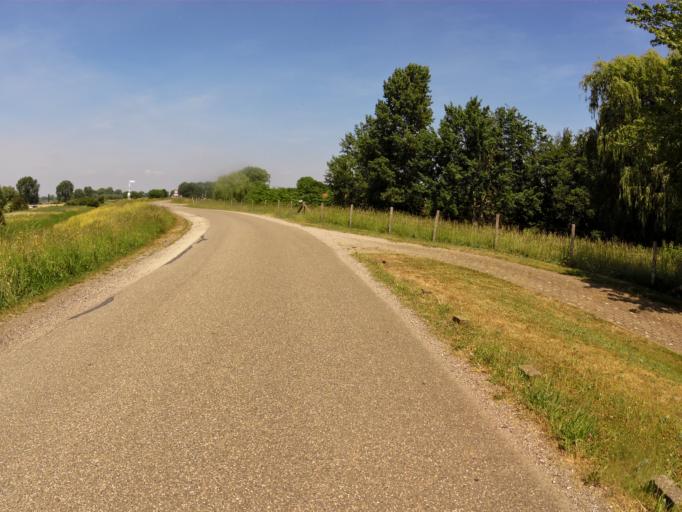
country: NL
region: Gelderland
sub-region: Gemeente Maasdriel
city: Heerewaarden
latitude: 51.7605
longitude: 5.3639
